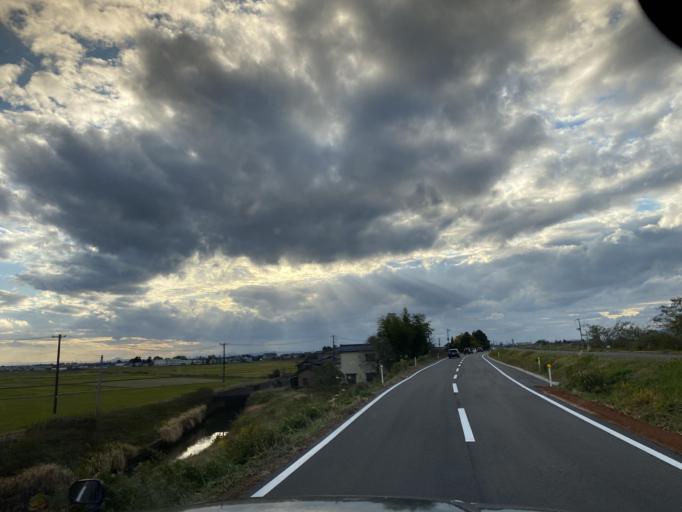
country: JP
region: Niigata
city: Kamo
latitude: 37.6677
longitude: 139.0053
